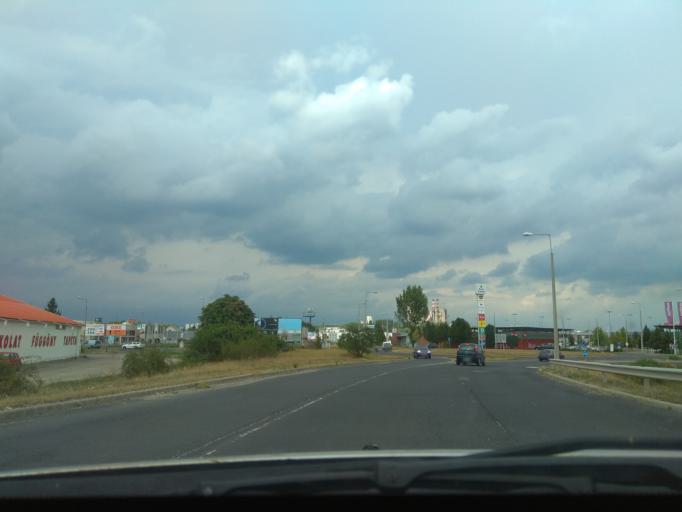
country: HU
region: Borsod-Abauj-Zemplen
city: Miskolc
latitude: 48.0541
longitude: 20.7995
